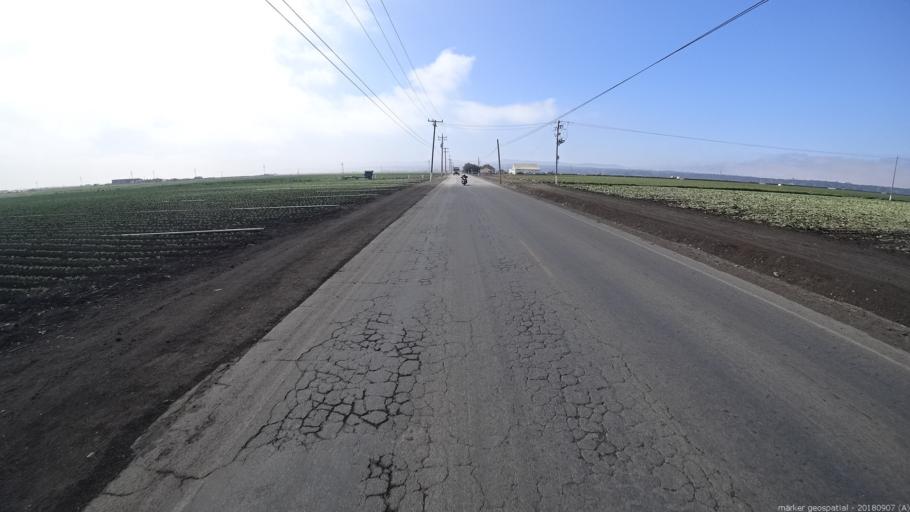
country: US
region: California
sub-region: Monterey County
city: Boronda
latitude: 36.6962
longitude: -121.7349
